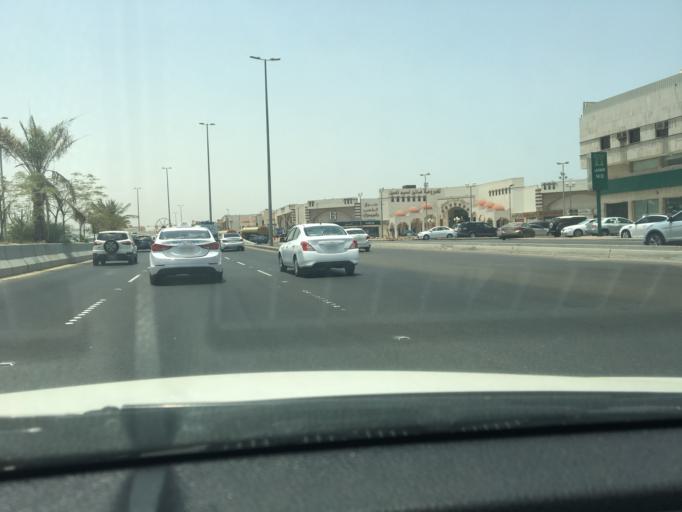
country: SA
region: Makkah
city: Jeddah
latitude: 21.5706
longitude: 39.1814
